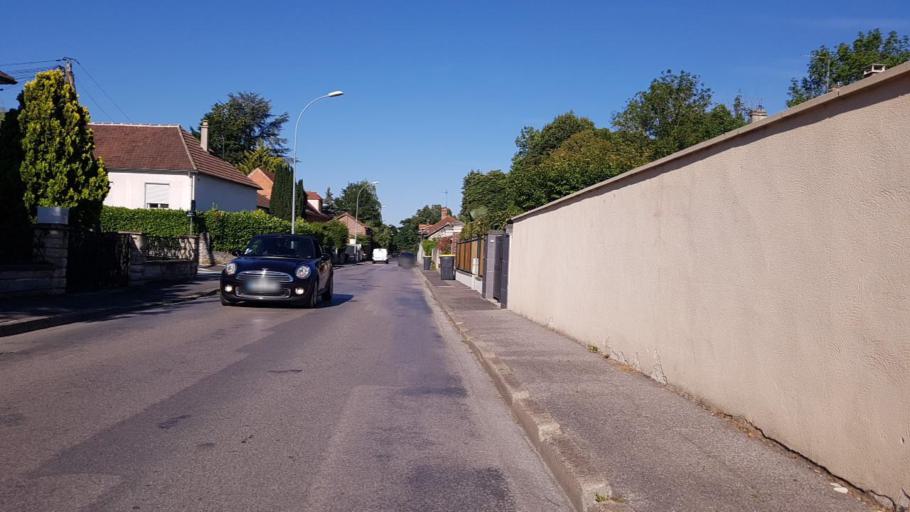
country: FR
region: Picardie
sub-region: Departement de l'Oise
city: Senlis
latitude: 49.2112
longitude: 2.5964
